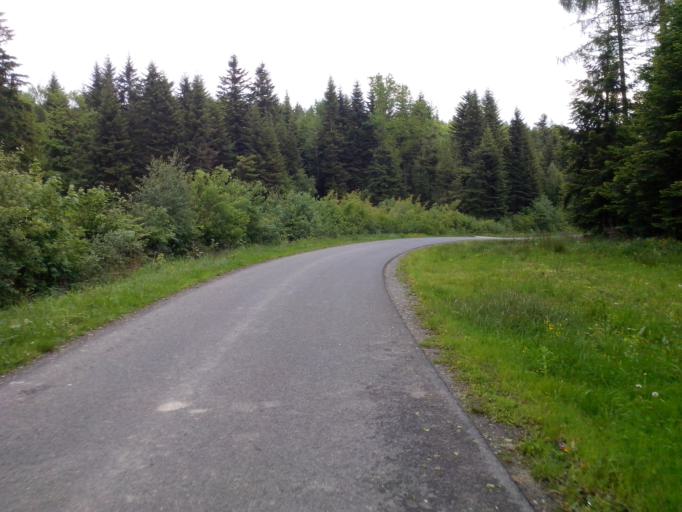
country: PL
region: Subcarpathian Voivodeship
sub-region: Powiat strzyzowski
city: Wysoka Strzyzowska
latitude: 49.8242
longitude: 21.7836
